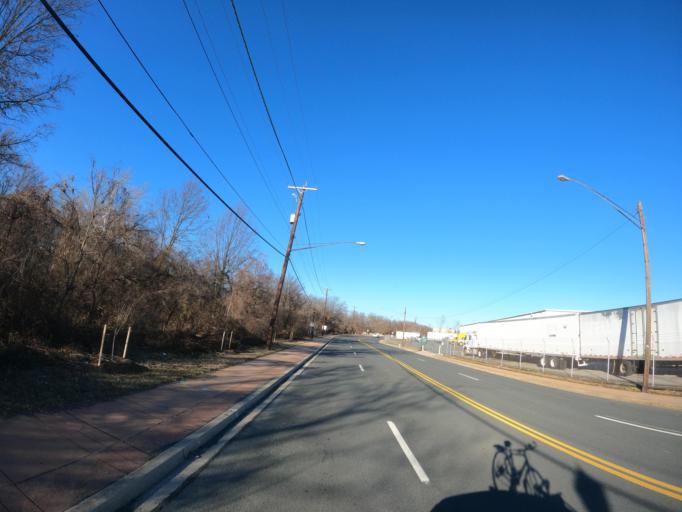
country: US
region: Maryland
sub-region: Prince George's County
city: Landover
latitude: 38.9298
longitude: -76.8926
